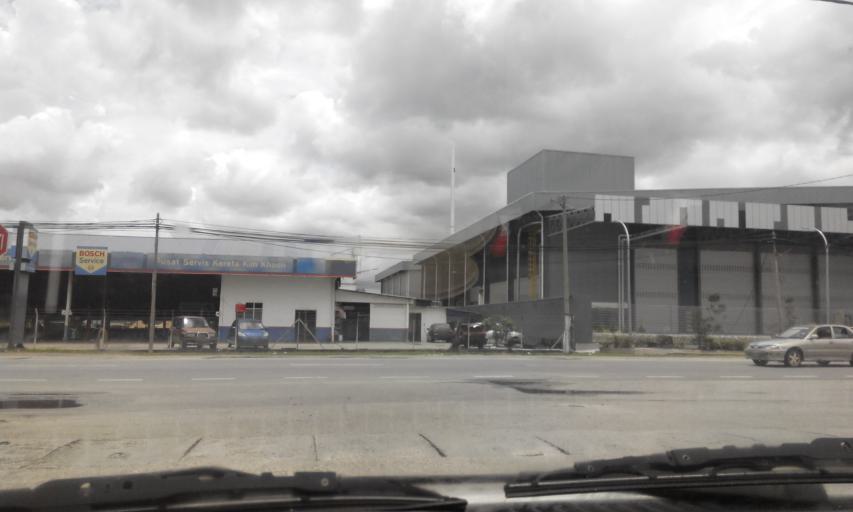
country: MY
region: Perak
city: Parit Buntar
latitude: 5.1081
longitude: 100.4894
